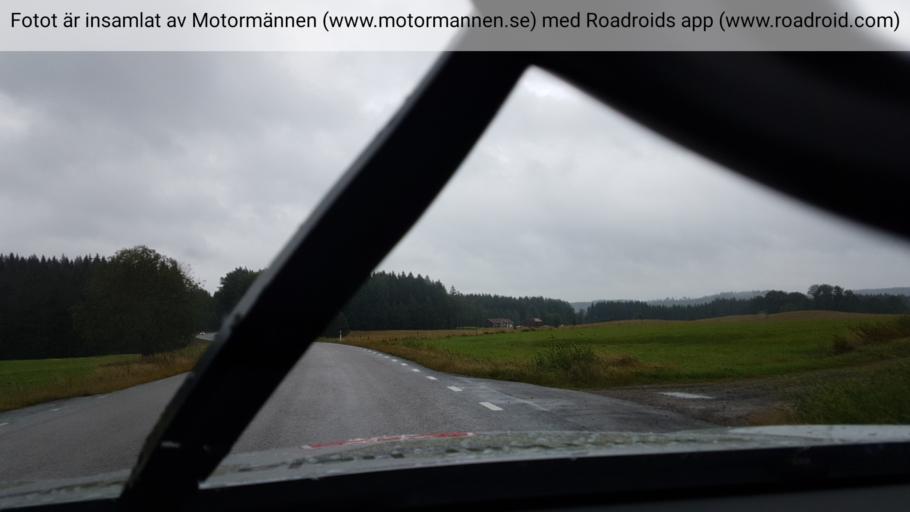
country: SE
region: Vaestra Goetaland
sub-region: Dals-Ed Kommun
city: Ed
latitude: 58.8809
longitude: 11.9015
